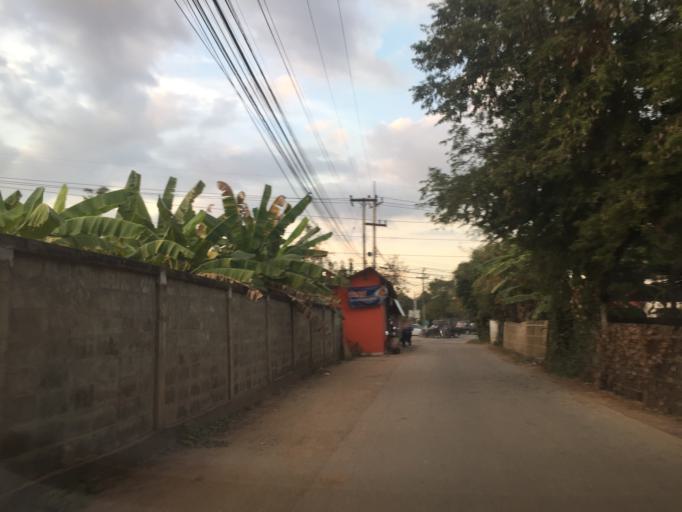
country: TH
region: Lamphun
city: Lamphun
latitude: 18.5256
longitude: 99.0170
